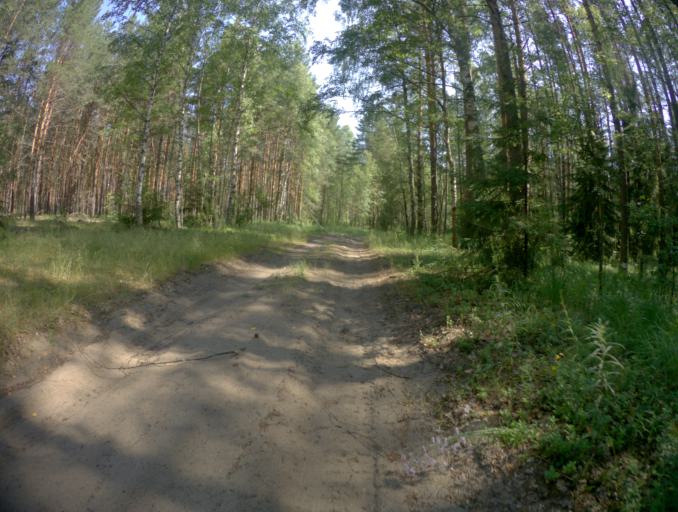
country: RU
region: Vladimir
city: Vyazniki
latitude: 56.3799
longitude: 42.2457
